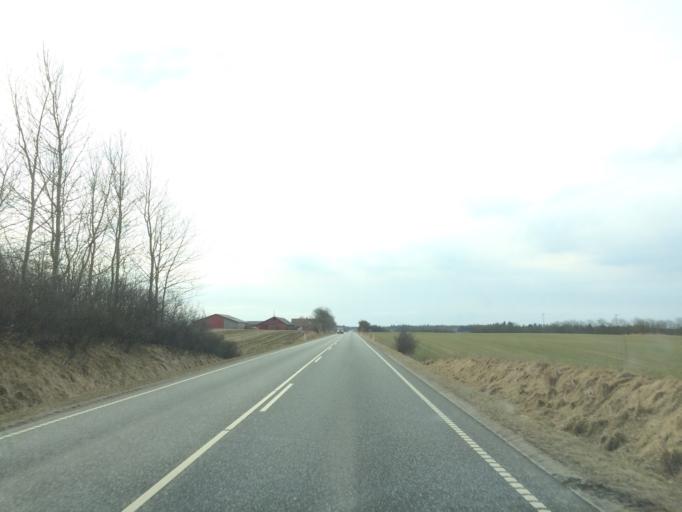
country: DK
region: Central Jutland
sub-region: Ringkobing-Skjern Kommune
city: Videbaek
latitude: 56.1040
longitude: 8.5079
